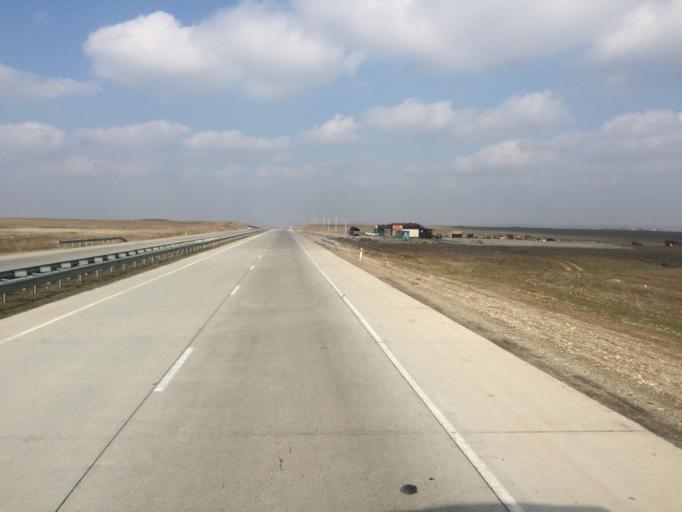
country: KZ
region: Ongtustik Qazaqstan
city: Temirlanovka
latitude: 42.5672
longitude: 69.3109
